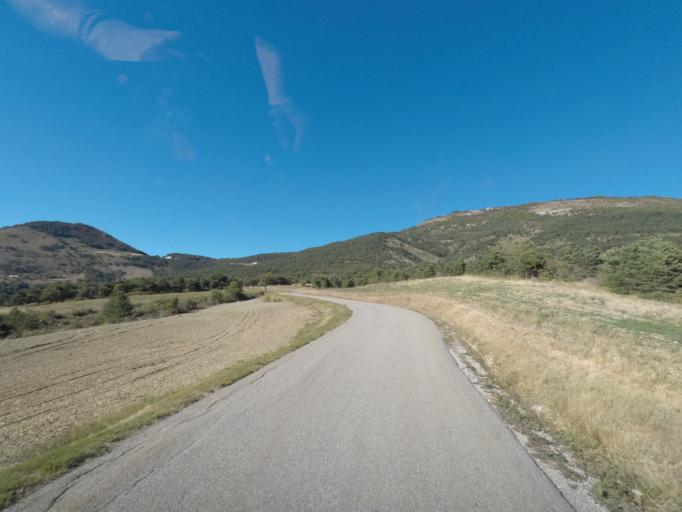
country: FR
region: Provence-Alpes-Cote d'Azur
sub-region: Departement des Hautes-Alpes
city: Serres
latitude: 44.4235
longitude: 5.5817
